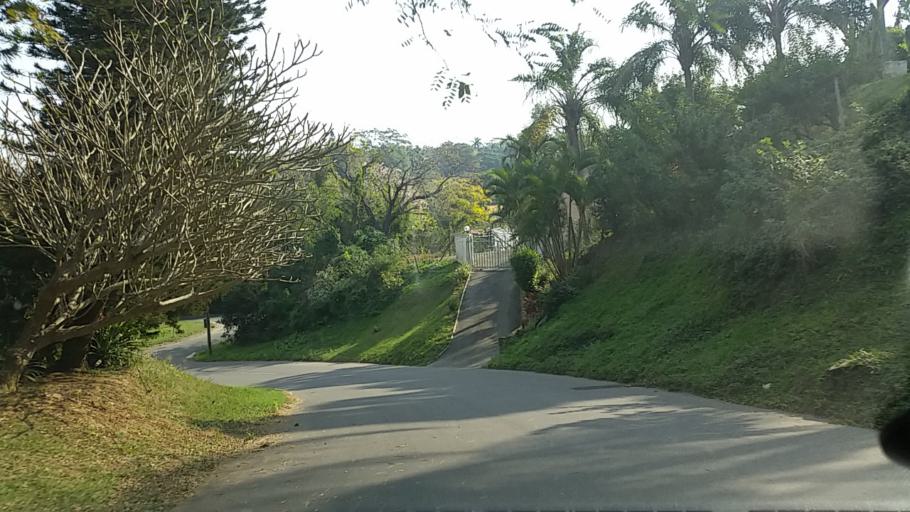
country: ZA
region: KwaZulu-Natal
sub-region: eThekwini Metropolitan Municipality
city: Berea
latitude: -29.8379
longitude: 30.9539
